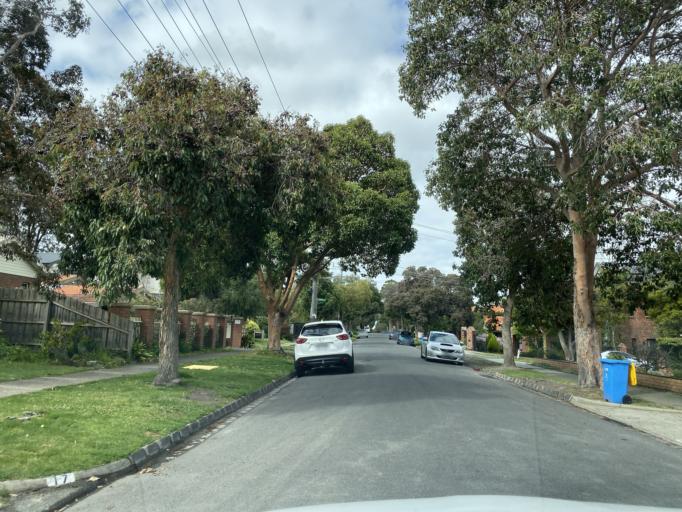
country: AU
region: Victoria
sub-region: Boroondara
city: Ashburton
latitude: -37.8514
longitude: 145.0897
